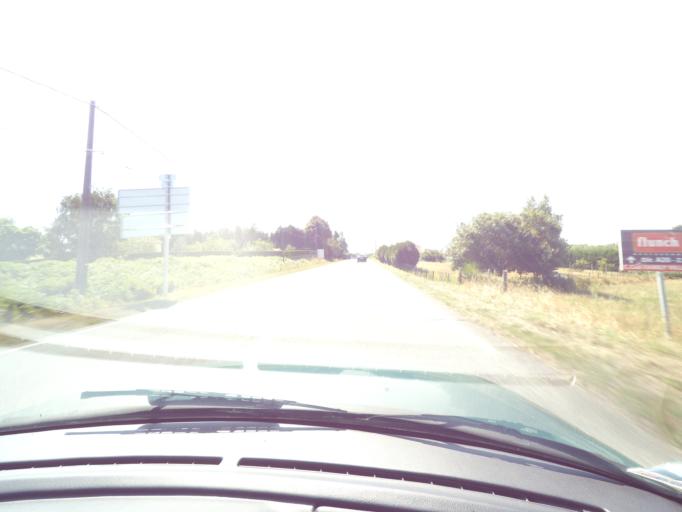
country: FR
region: Limousin
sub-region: Departement de la Haute-Vienne
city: Chaptelat
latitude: 45.9084
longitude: 1.2208
